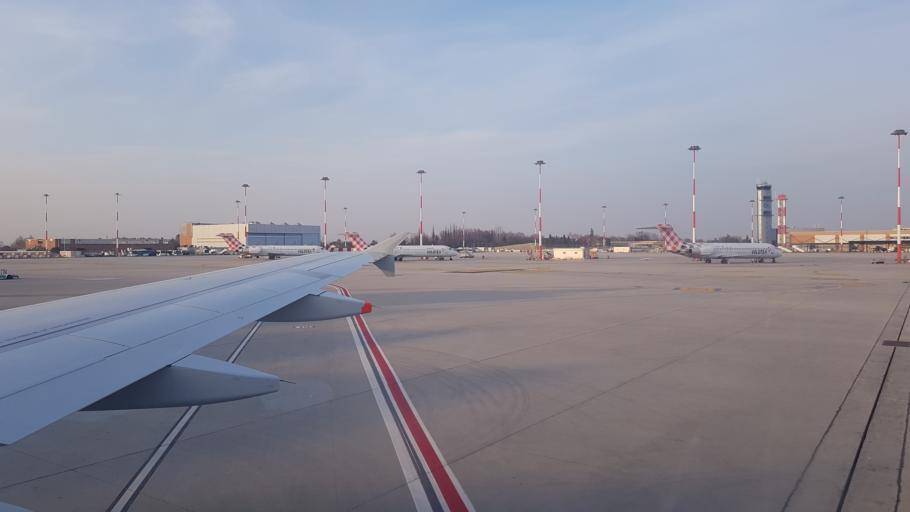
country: IT
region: Veneto
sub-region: Provincia di Venezia
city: Tessera
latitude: 45.5056
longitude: 12.3428
